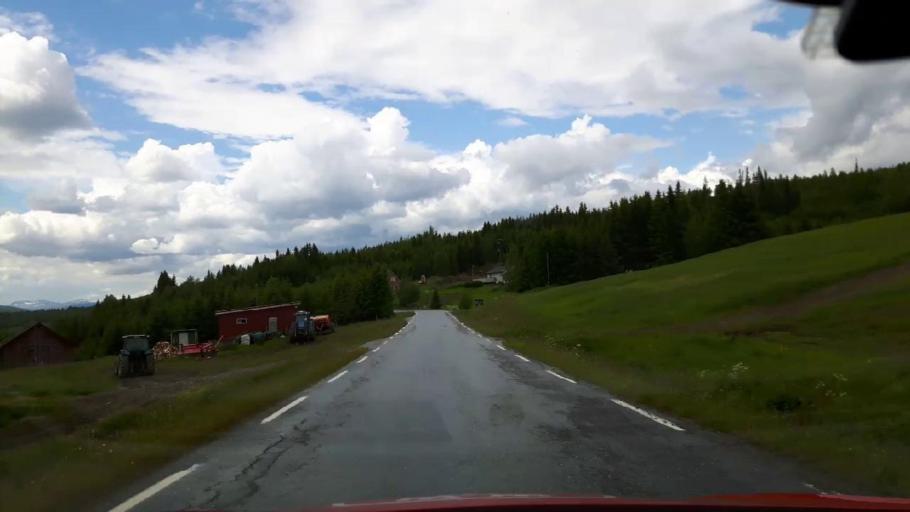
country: NO
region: Nord-Trondelag
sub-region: Lierne
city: Sandvika
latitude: 64.1086
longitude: 13.9821
